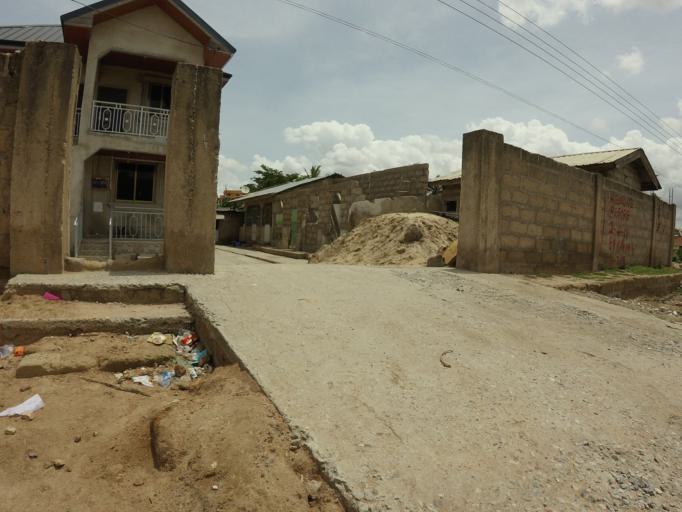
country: GH
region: Greater Accra
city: Dome
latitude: 5.6137
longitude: -0.2439
